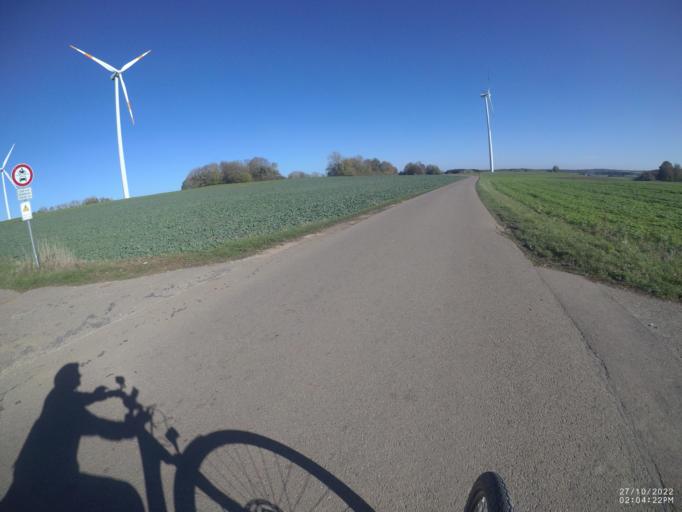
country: DE
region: Baden-Wuerttemberg
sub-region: Regierungsbezirk Stuttgart
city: Deggingen
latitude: 48.5757
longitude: 9.7475
